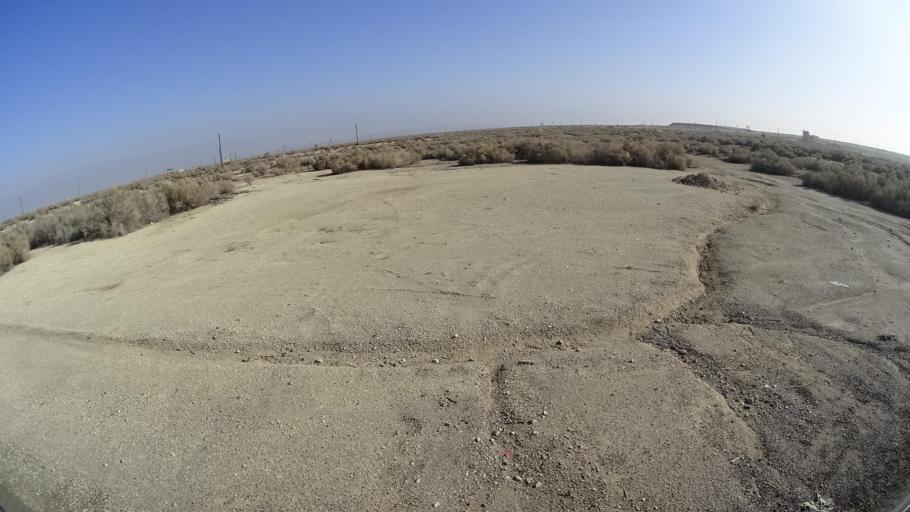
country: US
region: California
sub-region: Kern County
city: Taft Heights
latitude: 35.1988
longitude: -119.5683
